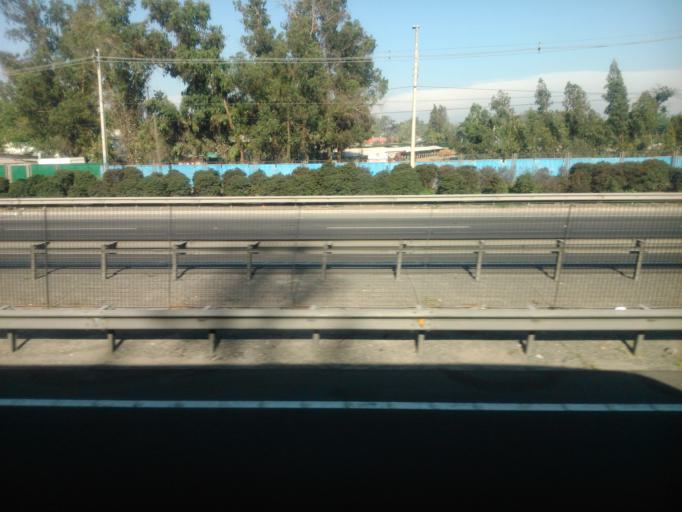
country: CL
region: Santiago Metropolitan
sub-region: Provincia de Maipo
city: San Bernardo
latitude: -33.6348
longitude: -70.7130
